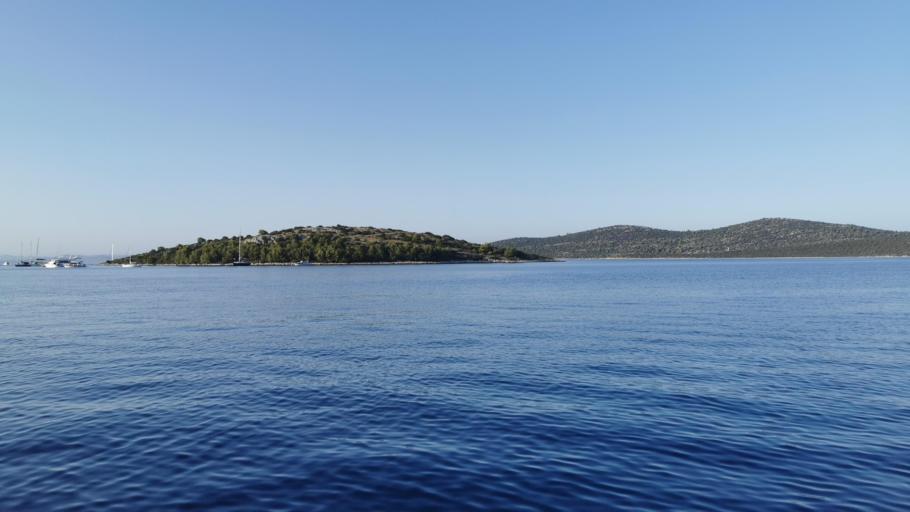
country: HR
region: Sibensko-Kniniska
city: Tribunj
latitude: 43.6938
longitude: 15.6674
